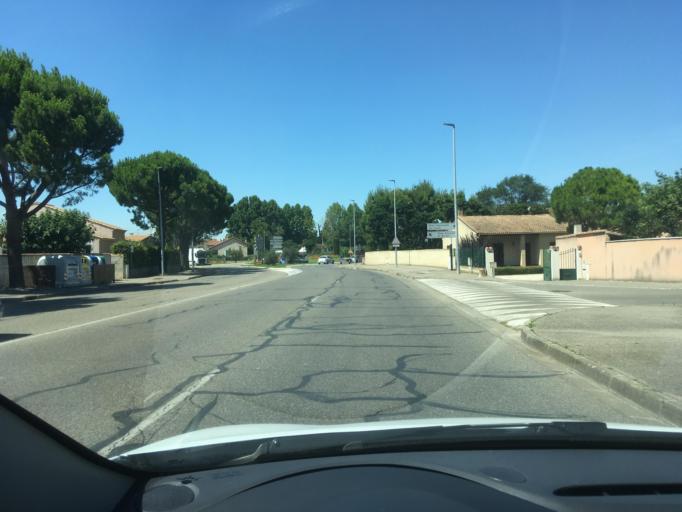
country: FR
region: Provence-Alpes-Cote d'Azur
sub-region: Departement des Bouches-du-Rhone
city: Chateaurenard
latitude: 43.8844
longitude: 4.8624
